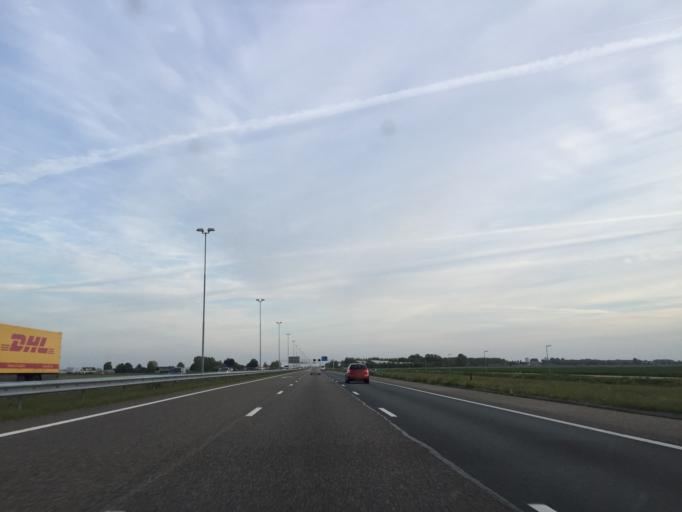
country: NL
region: North Holland
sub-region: Gemeente Haarlemmermeer
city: Hoofddorp
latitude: 52.3439
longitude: 4.7353
